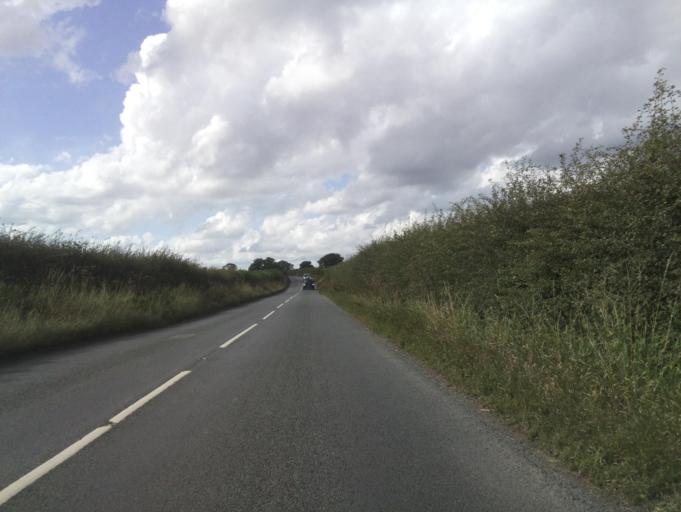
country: GB
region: England
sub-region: North Yorkshire
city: Bedale
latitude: 54.2079
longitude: -1.6052
